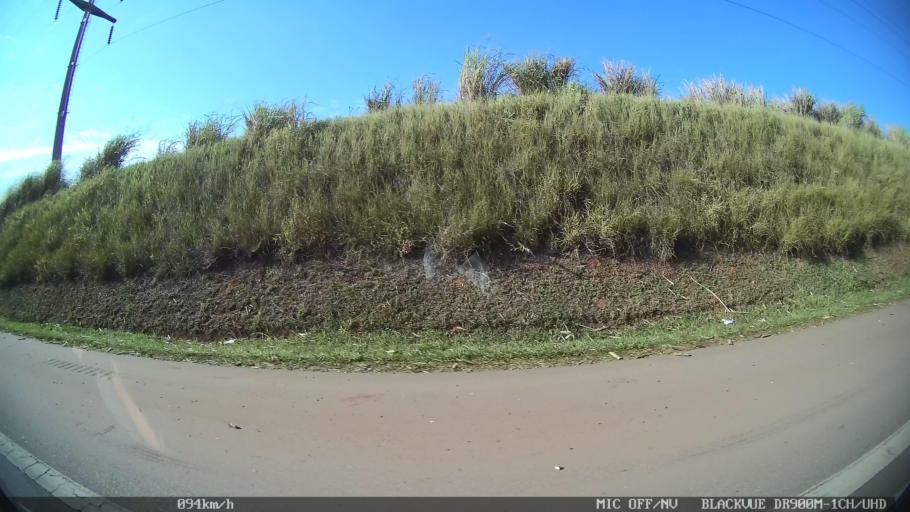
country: BR
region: Sao Paulo
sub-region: Piracicaba
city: Piracicaba
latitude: -22.6780
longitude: -47.5967
